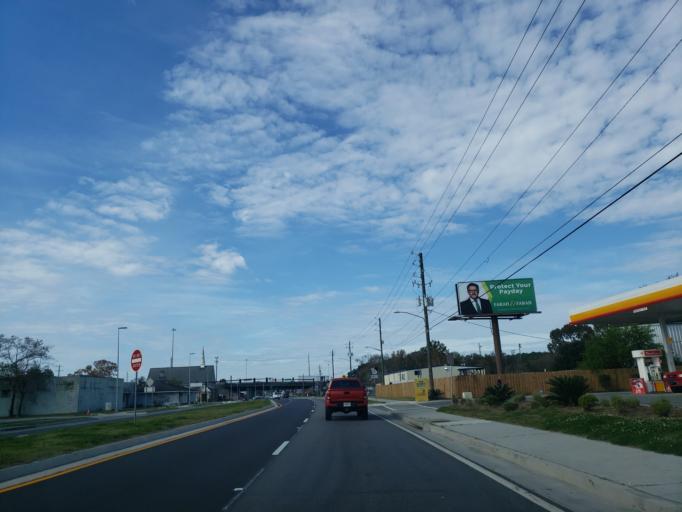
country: US
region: Georgia
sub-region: Chatham County
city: Savannah
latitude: 32.0899
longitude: -81.1240
